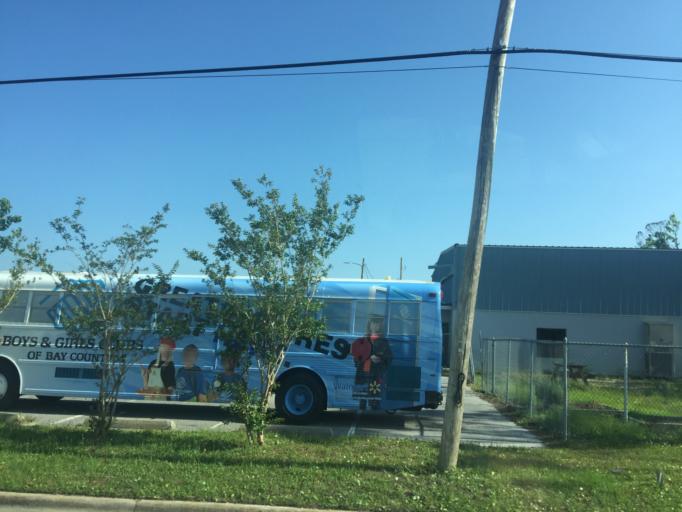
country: US
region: Florida
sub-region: Bay County
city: Springfield
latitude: 30.1531
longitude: -85.6214
